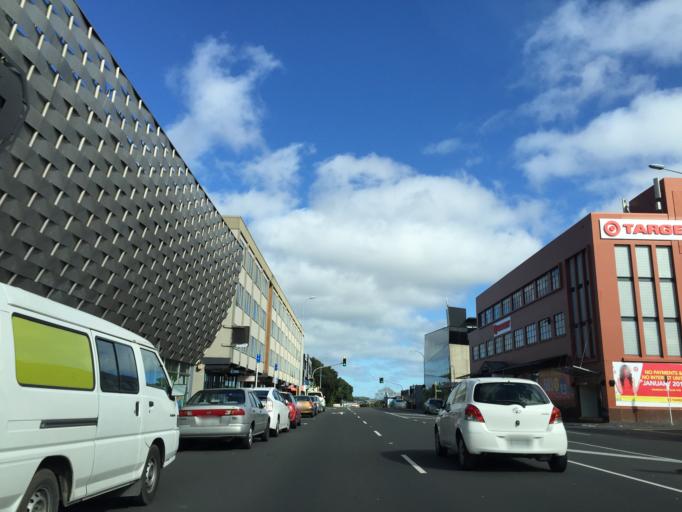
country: NZ
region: Auckland
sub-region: Auckland
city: Auckland
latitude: -36.8712
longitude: 174.7526
